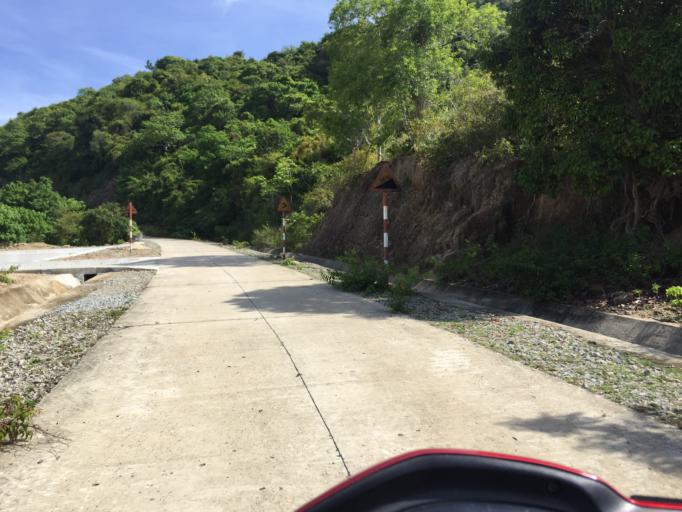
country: VN
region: Quang Nam
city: Hoi An
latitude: 15.9335
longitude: 108.5312
